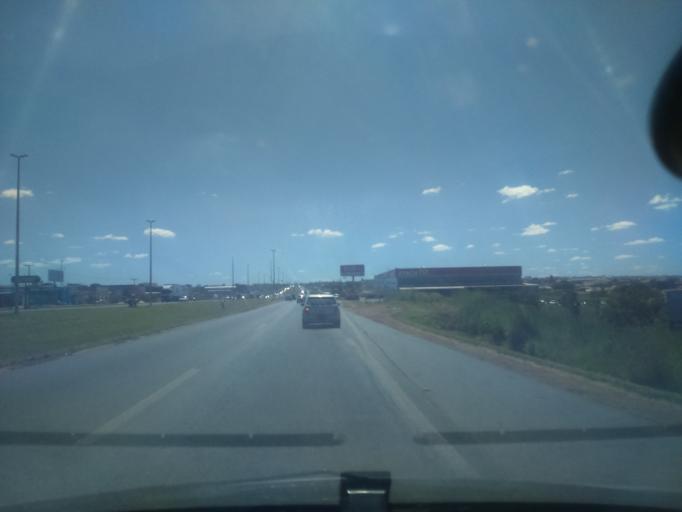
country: BR
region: Goias
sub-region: Luziania
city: Luziania
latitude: -16.1126
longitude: -47.9694
